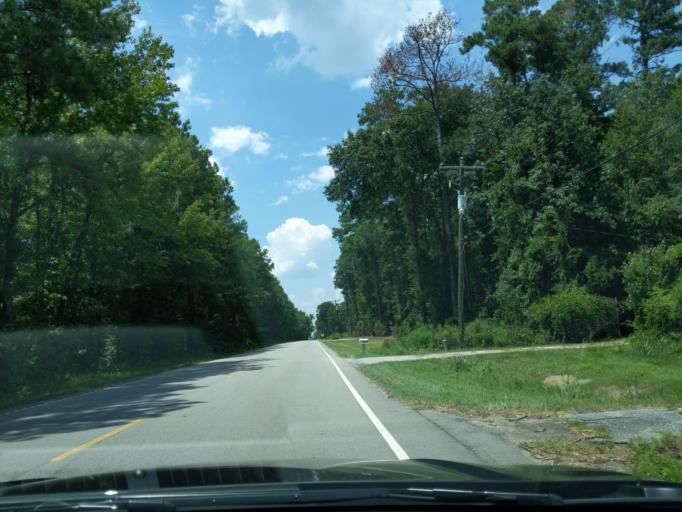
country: US
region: South Carolina
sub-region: Richland County
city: Hopkins
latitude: 33.9075
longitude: -80.9336
